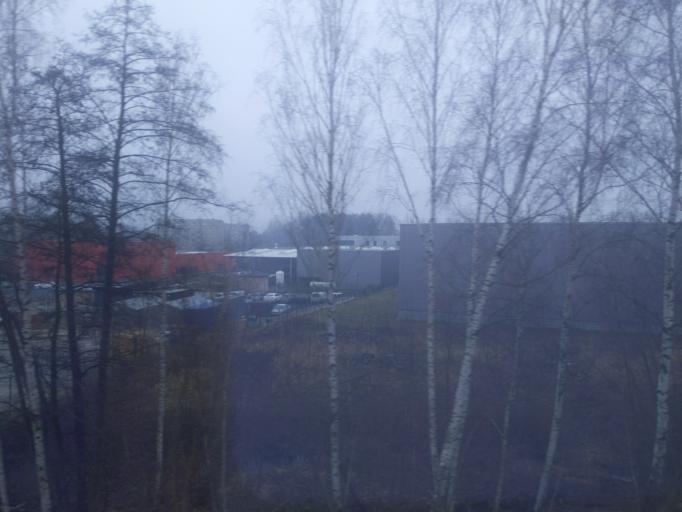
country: DE
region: Saxony
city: Albertstadt
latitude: 51.1278
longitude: 13.7902
